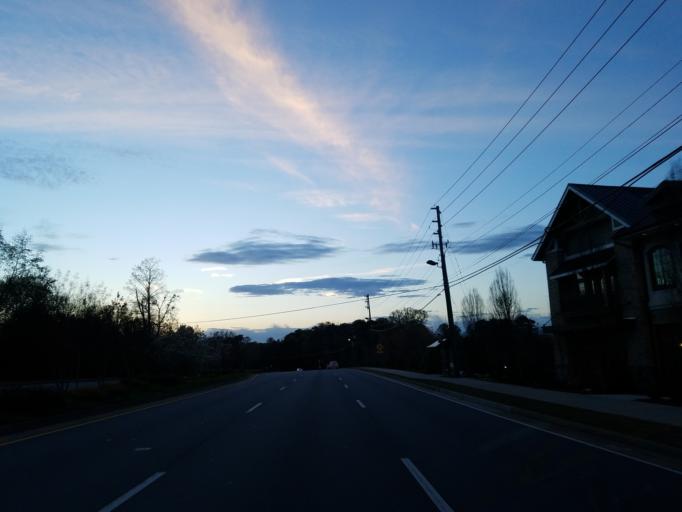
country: US
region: Georgia
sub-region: Fulton County
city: Alpharetta
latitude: 34.0696
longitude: -84.2847
